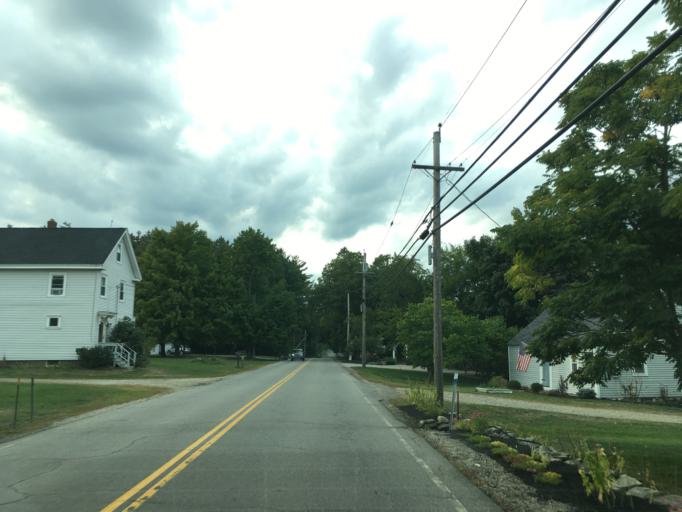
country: US
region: New Hampshire
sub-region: Rockingham County
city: Stratham Station
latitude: 43.0071
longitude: -70.9055
